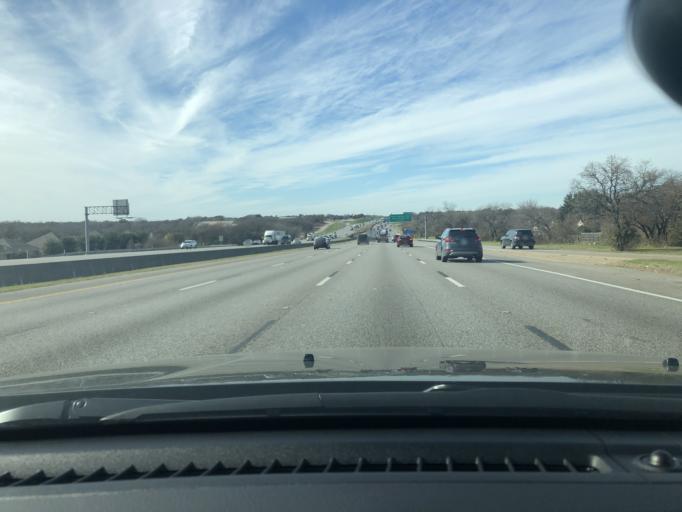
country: US
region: Texas
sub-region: Tarrant County
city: Dalworthington Gardens
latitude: 32.6748
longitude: -97.1537
